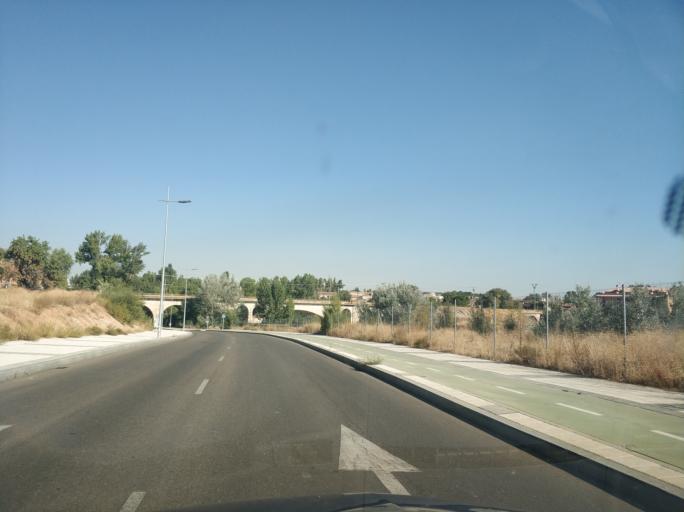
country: ES
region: Castille and Leon
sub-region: Provincia de Burgos
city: Aranda de Duero
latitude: 41.6713
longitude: -3.6942
